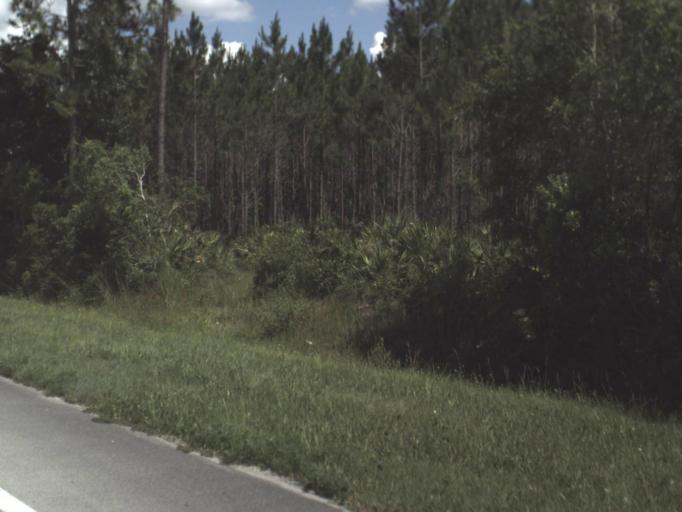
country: US
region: Florida
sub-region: Clay County
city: Keystone Heights
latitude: 29.7128
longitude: -82.0956
